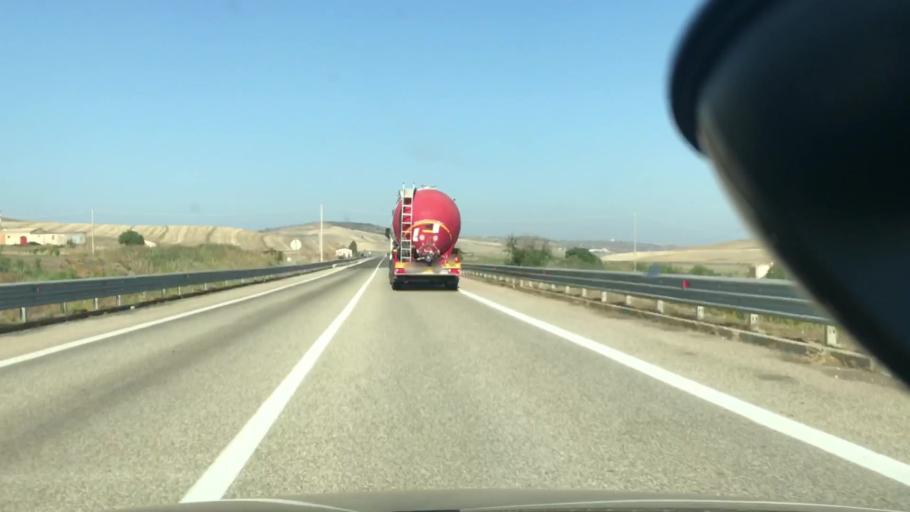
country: IT
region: Basilicate
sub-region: Provincia di Matera
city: Irsina
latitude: 40.7847
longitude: 16.2999
